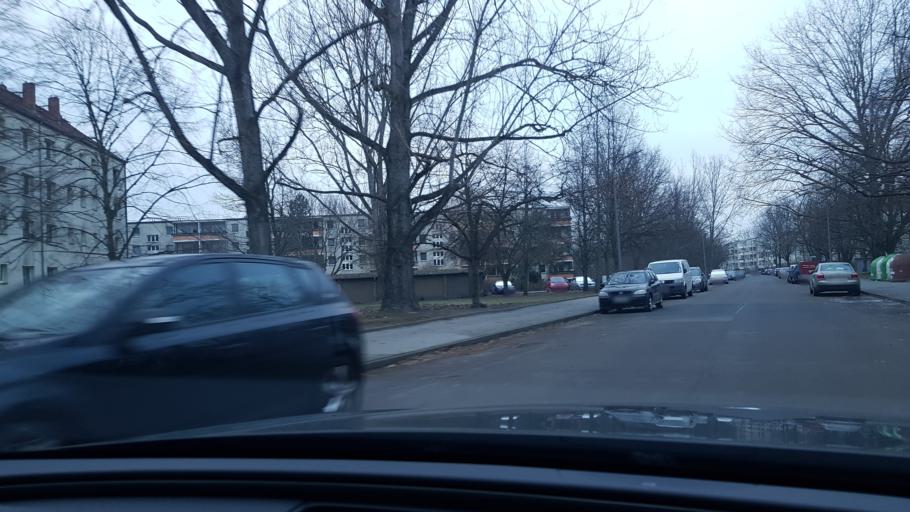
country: DE
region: Berlin
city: Grunau
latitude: 52.4242
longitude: 13.5918
